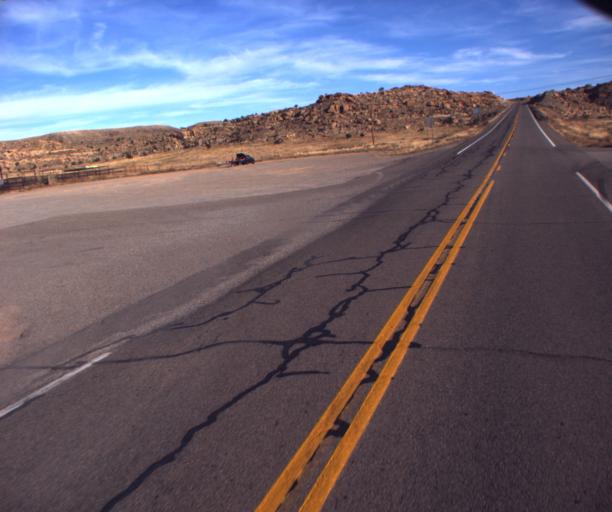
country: US
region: New Mexico
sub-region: San Juan County
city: Shiprock
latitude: 36.9194
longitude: -109.0847
